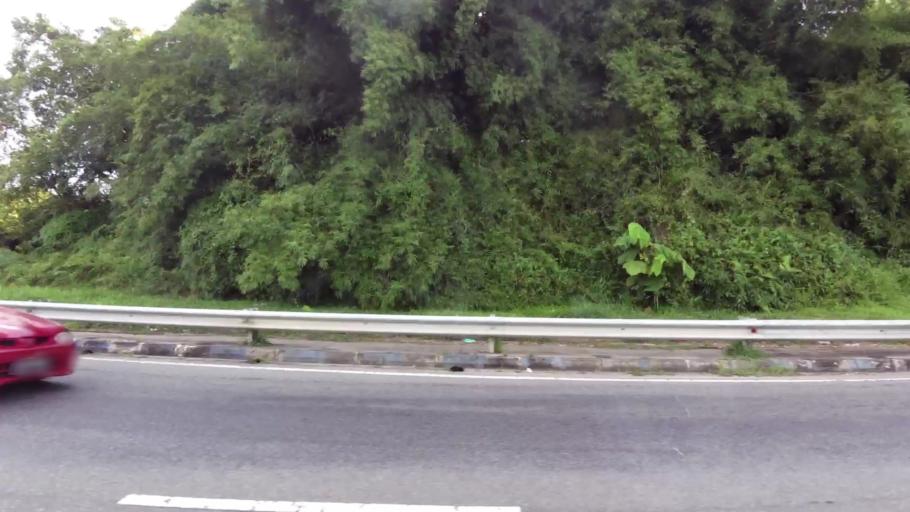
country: BN
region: Brunei and Muara
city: Bandar Seri Begawan
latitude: 4.9714
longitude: 115.0210
